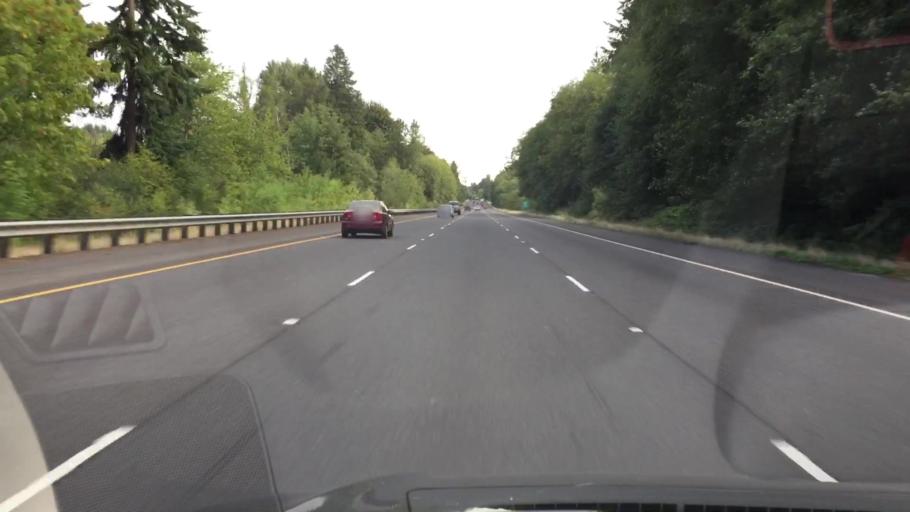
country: US
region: Washington
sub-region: Cowlitz County
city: West Side Highway
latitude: 46.2239
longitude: -122.8900
